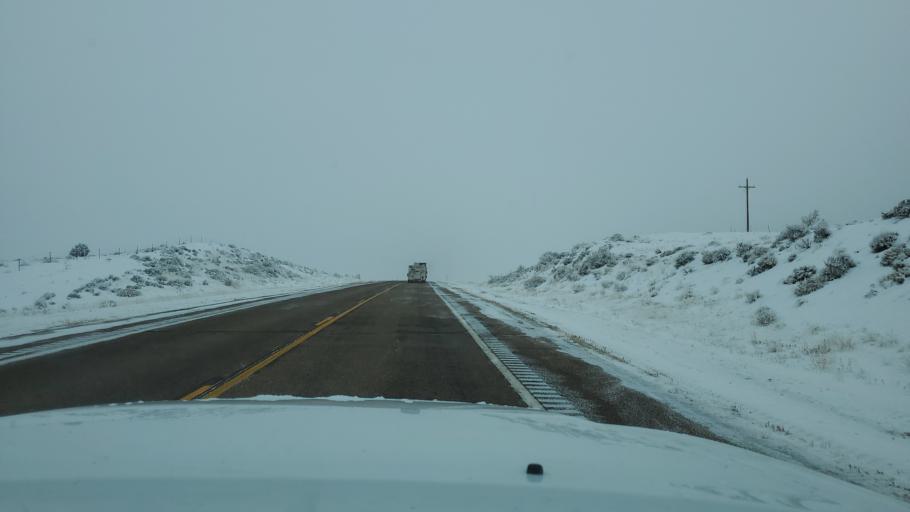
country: US
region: Colorado
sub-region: Rio Blanco County
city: Rangely
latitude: 40.2427
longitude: -108.9566
